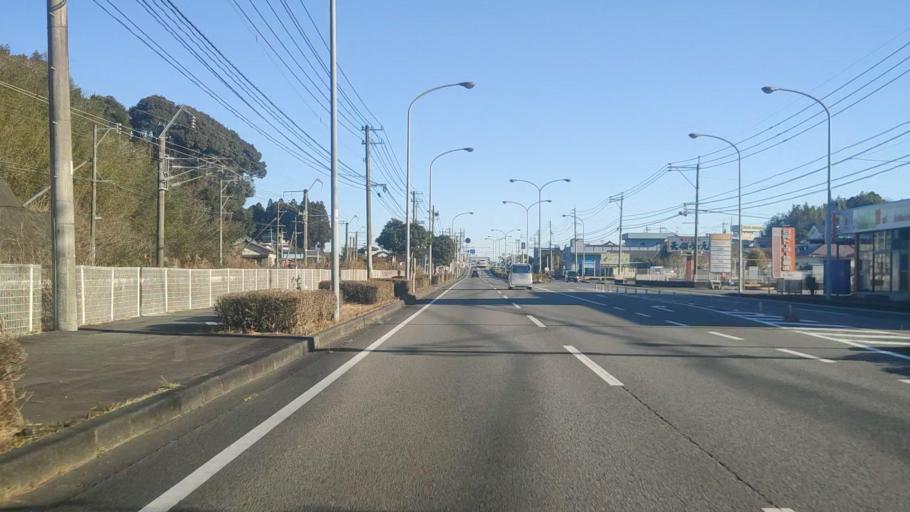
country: JP
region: Miyazaki
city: Nobeoka
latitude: 32.4551
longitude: 131.6433
